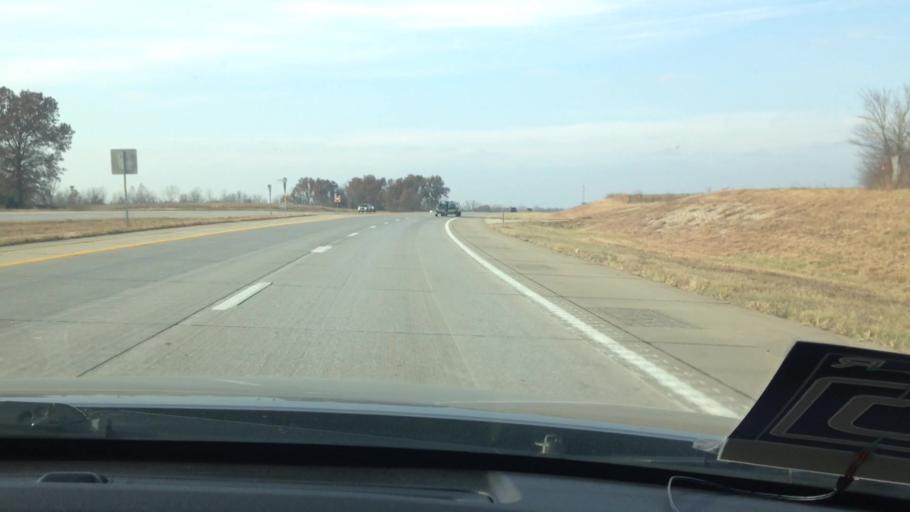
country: US
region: Missouri
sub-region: Henry County
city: Clinton
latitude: 38.4430
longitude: -93.9536
